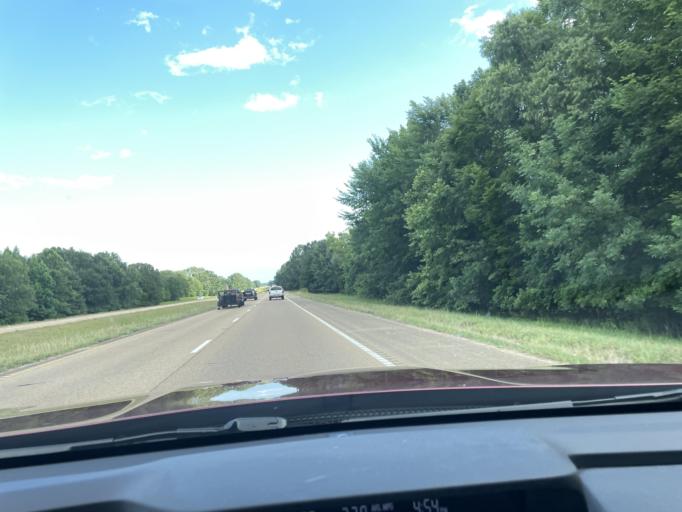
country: US
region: Mississippi
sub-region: Madison County
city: Flora
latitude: 32.5059
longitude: -90.3011
